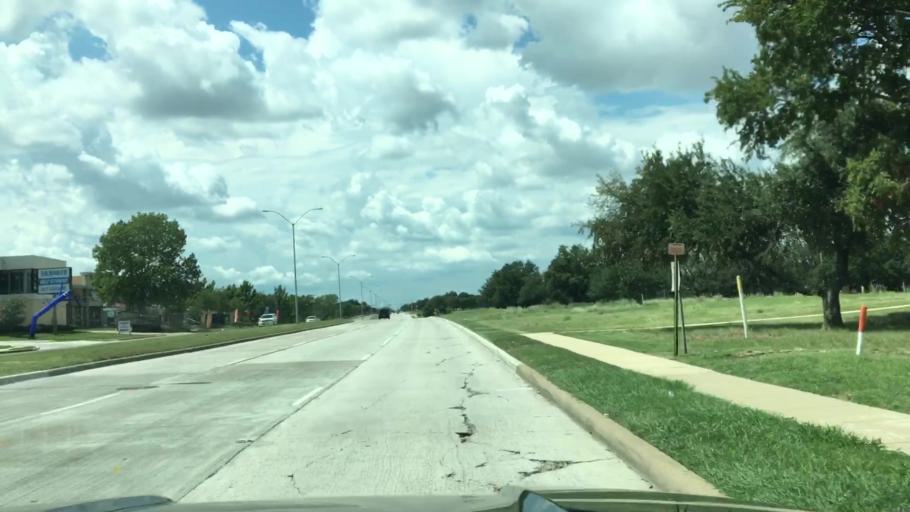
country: US
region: Texas
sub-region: Tarrant County
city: Blue Mound
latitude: 32.8613
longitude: -97.3186
